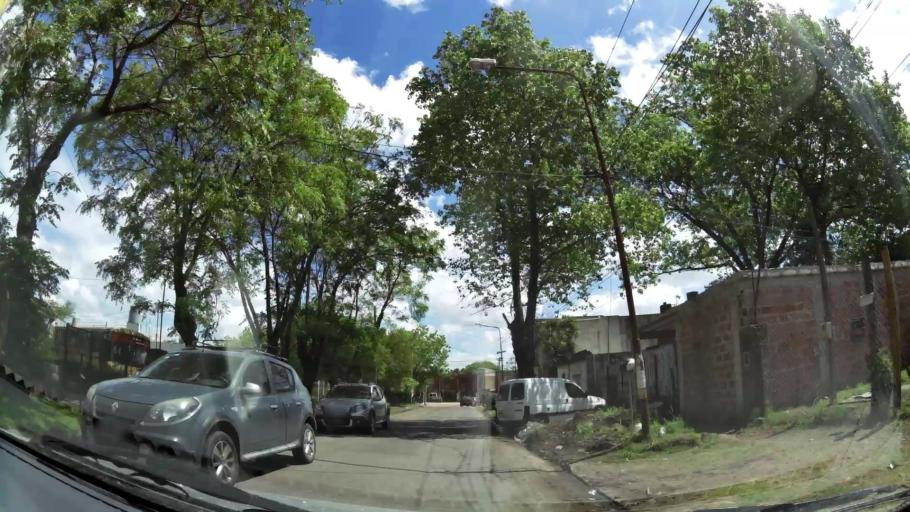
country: AR
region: Buenos Aires
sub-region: Partido de Quilmes
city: Quilmes
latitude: -34.8085
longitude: -58.2603
